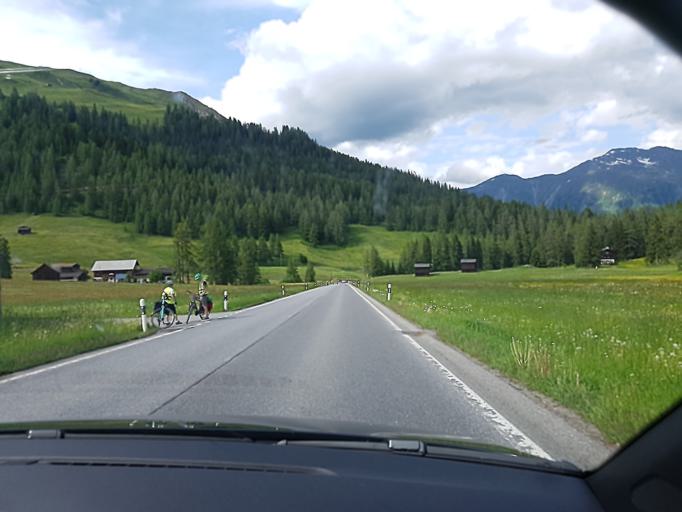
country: CH
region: Grisons
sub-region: Praettigau/Davos District
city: Davos
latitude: 46.8376
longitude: 9.8570
